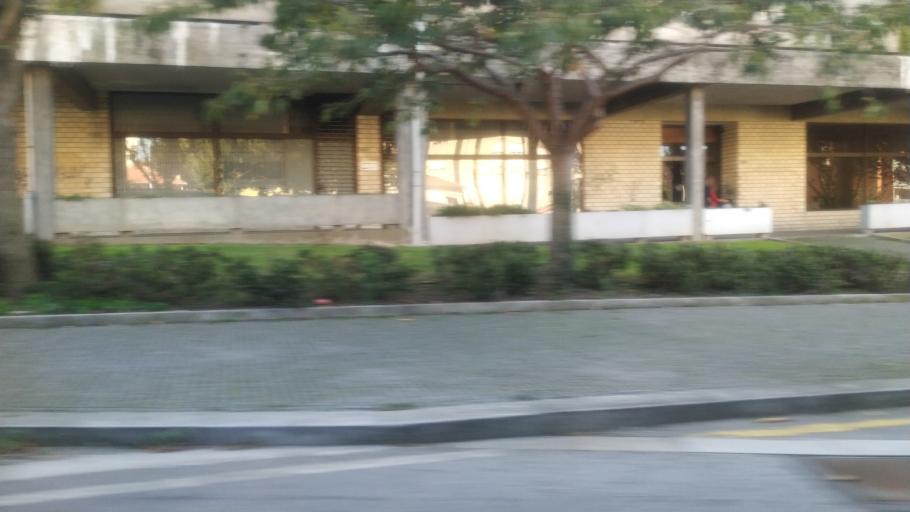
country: PT
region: Porto
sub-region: Matosinhos
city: Matosinhos
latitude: 41.1792
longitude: -8.6747
